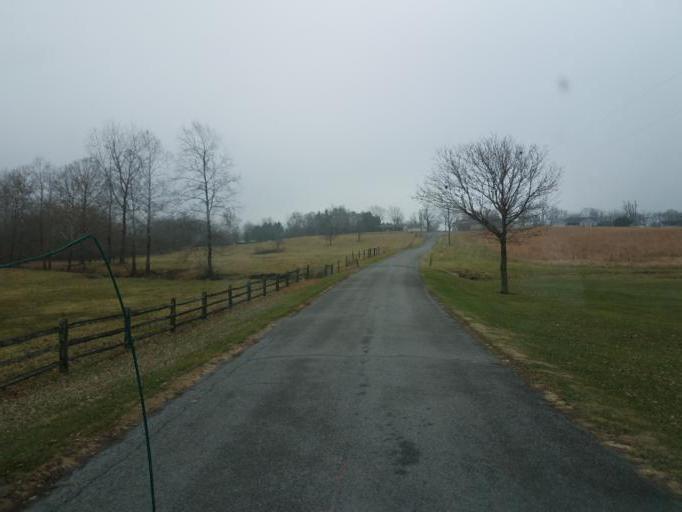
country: US
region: Ohio
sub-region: Champaign County
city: North Lewisburg
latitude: 40.2831
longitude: -83.5985
